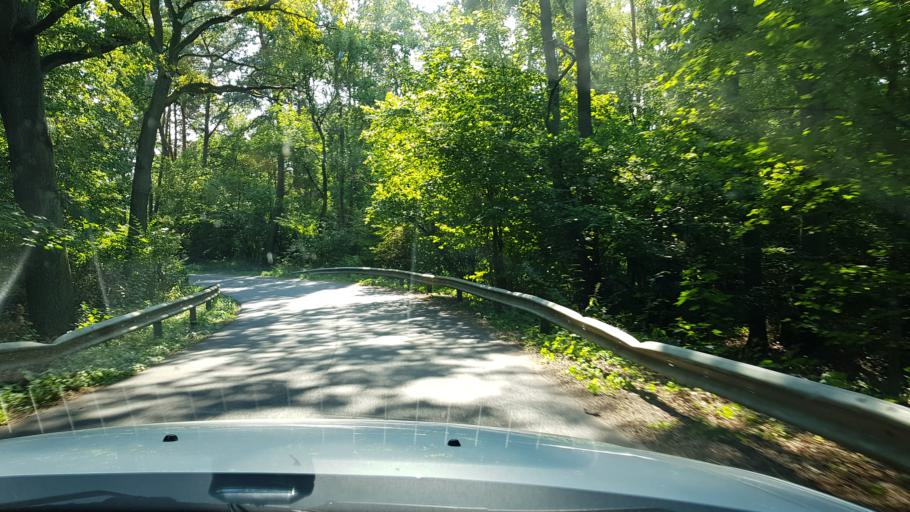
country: PL
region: West Pomeranian Voivodeship
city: Trzcinsko Zdroj
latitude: 52.9328
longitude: 14.5240
